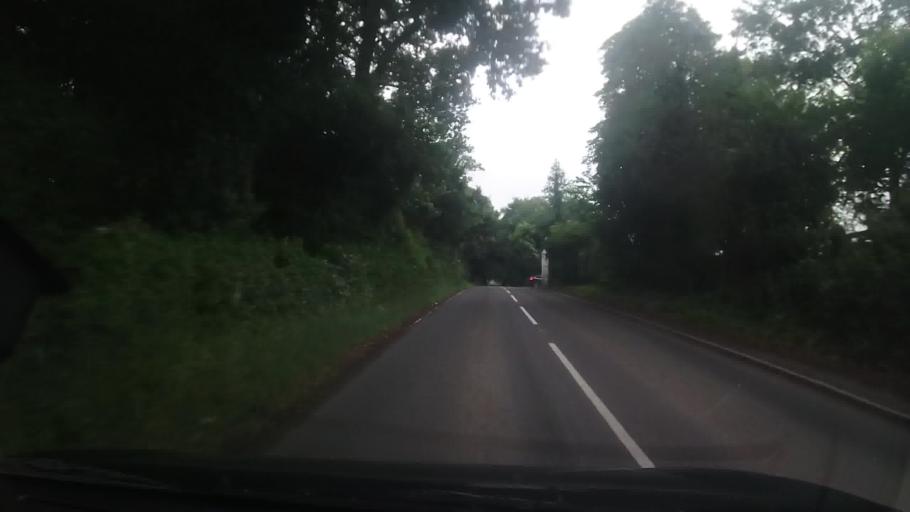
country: GB
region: England
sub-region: Shropshire
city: Shrewsbury
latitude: 52.7242
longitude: -2.7699
